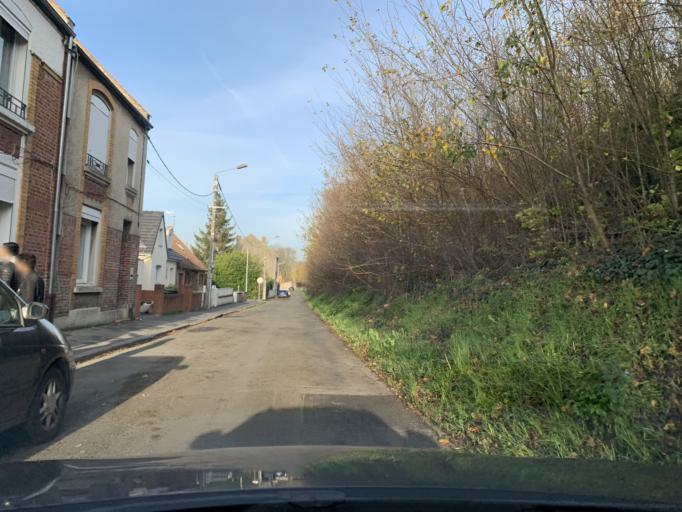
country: FR
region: Nord-Pas-de-Calais
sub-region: Departement du Nord
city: Cambrai
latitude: 50.1619
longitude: 3.2506
